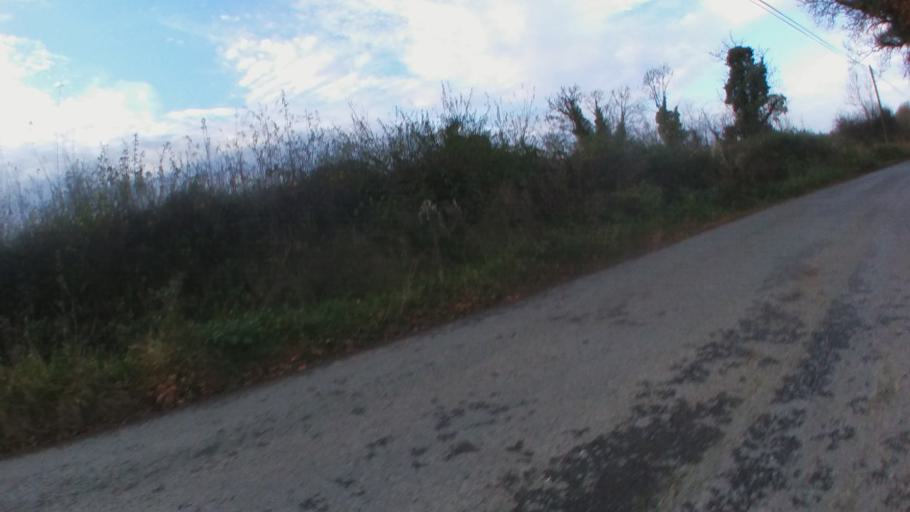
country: IE
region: Leinster
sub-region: Kilkenny
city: Kilkenny
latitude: 52.6922
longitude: -7.1720
